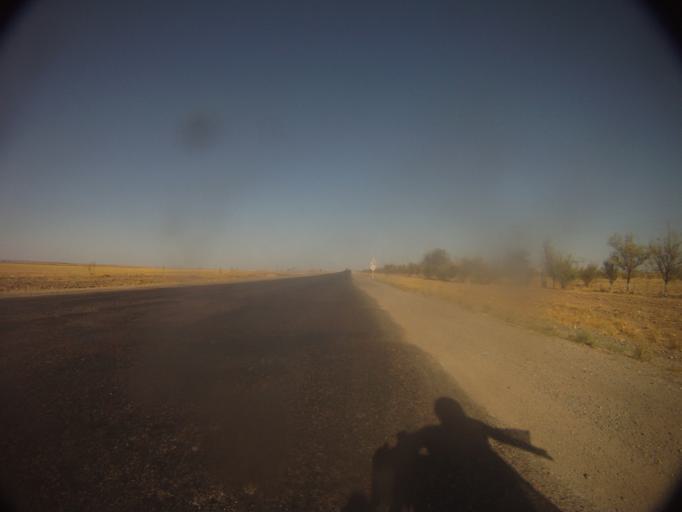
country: KZ
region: Zhambyl
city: Sarykemer
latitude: 42.9767
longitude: 71.5719
